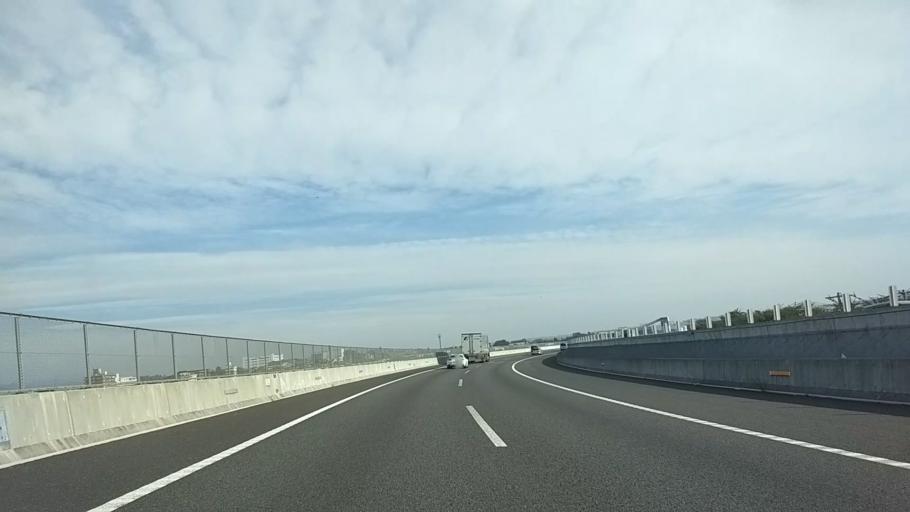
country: JP
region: Kanagawa
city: Atsugi
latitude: 35.4572
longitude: 139.3722
